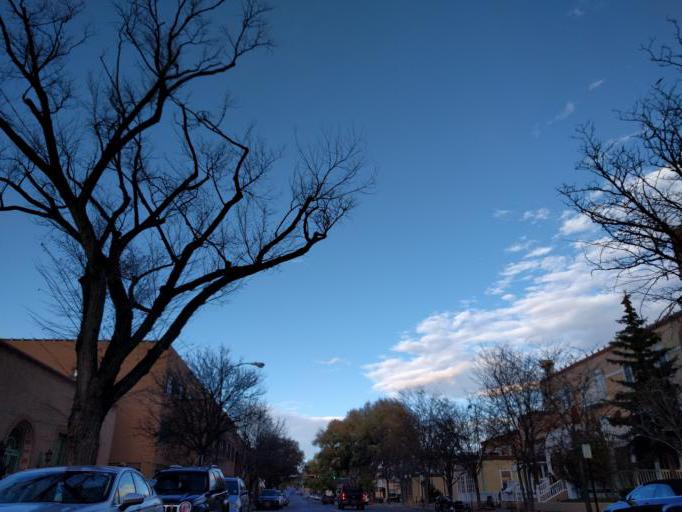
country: US
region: New Mexico
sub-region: Santa Fe County
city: Santa Fe
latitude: 35.6880
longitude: -105.9375
